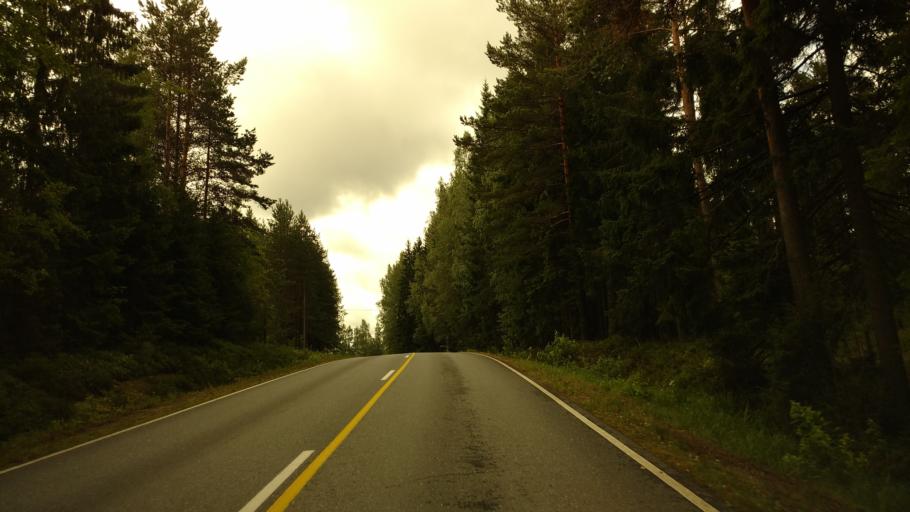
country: FI
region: Varsinais-Suomi
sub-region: Loimaa
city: Koski Tl
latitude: 60.5769
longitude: 23.1375
